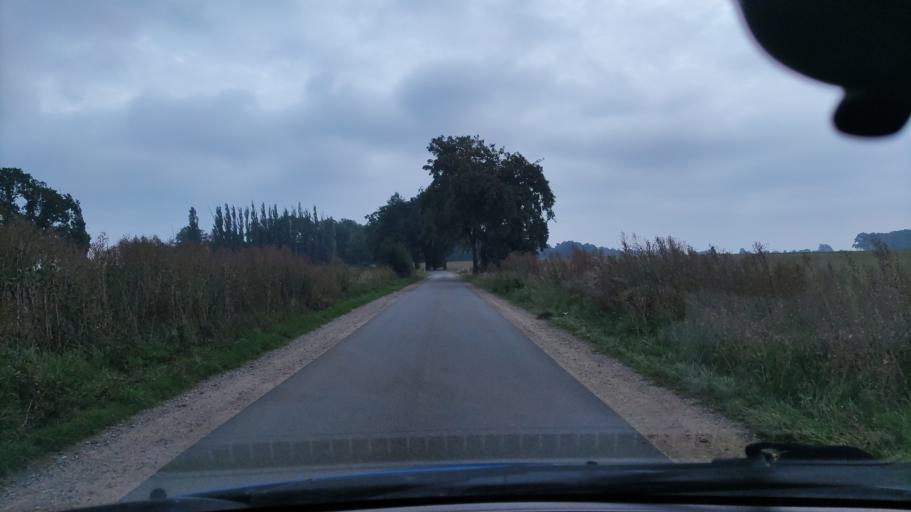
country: DE
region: Lower Saxony
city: Altenmedingen
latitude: 53.1271
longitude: 10.6168
